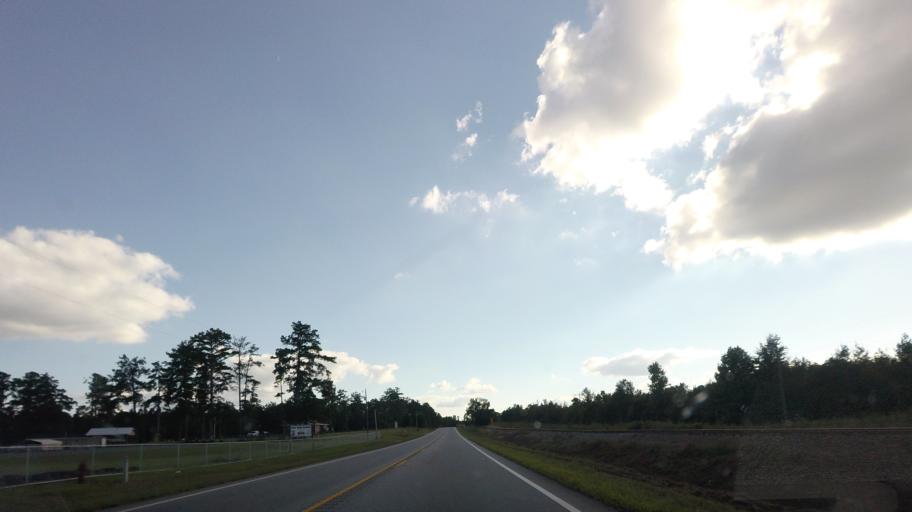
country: US
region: Georgia
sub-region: Lamar County
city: Barnesville
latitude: 33.0091
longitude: -84.1897
